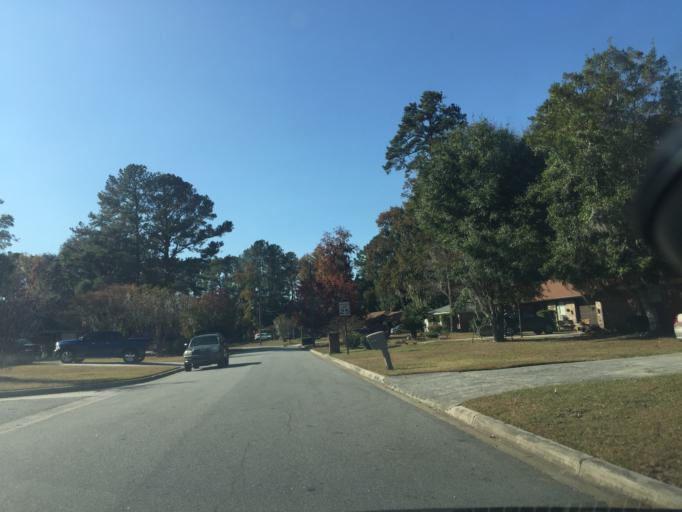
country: US
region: Georgia
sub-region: Chatham County
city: Montgomery
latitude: 31.9956
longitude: -81.1399
